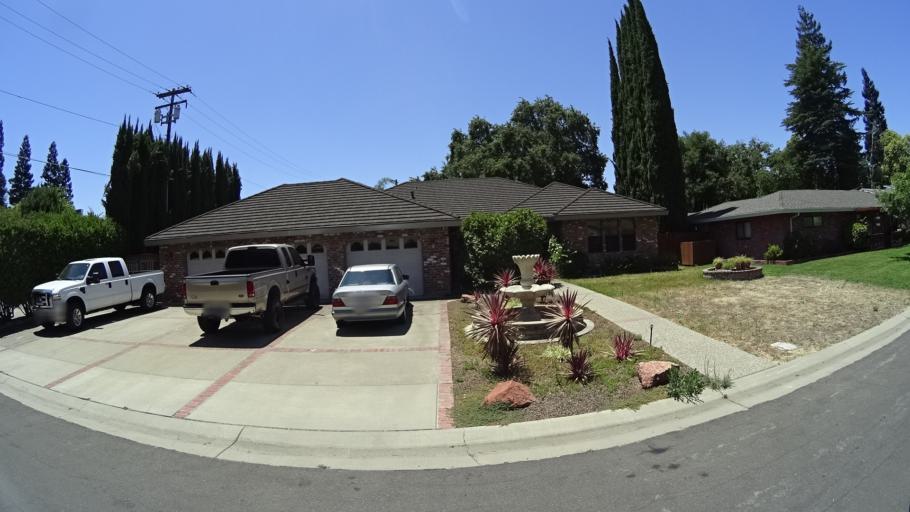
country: US
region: California
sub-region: Yolo County
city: West Sacramento
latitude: 38.5290
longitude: -121.5200
